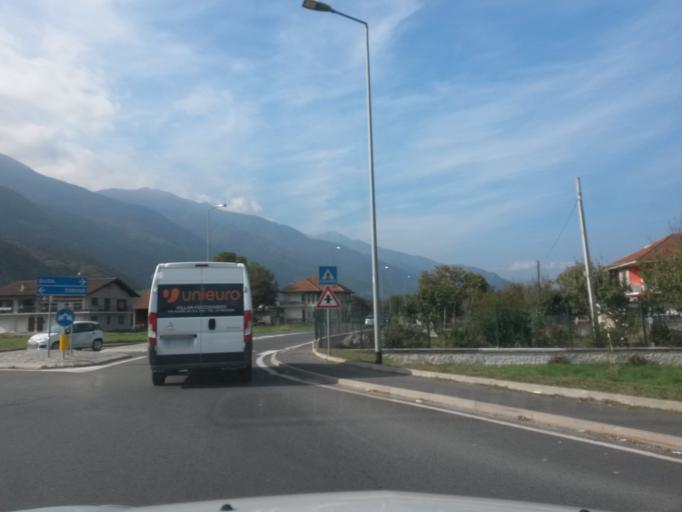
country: IT
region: Piedmont
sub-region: Provincia di Torino
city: Vaie
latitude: 45.1077
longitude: 7.2890
